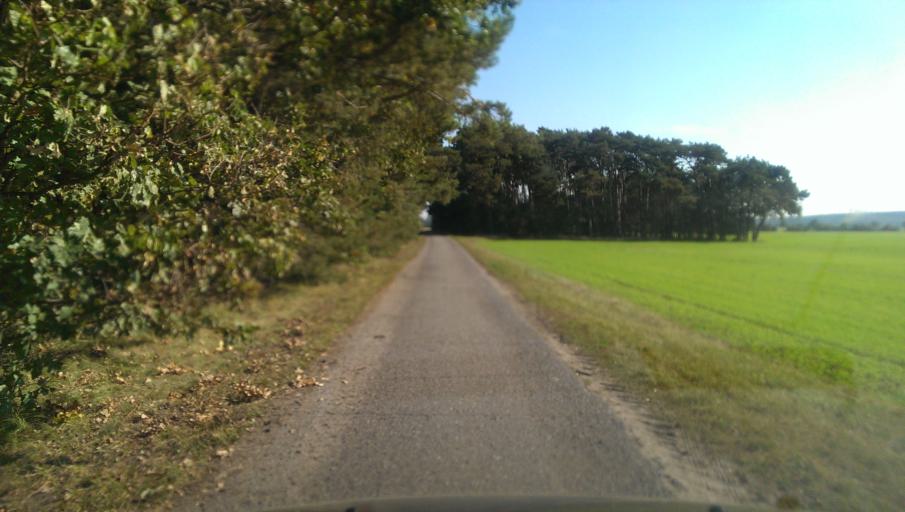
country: DE
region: Brandenburg
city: Am Mellensee
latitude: 52.2218
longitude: 13.3214
